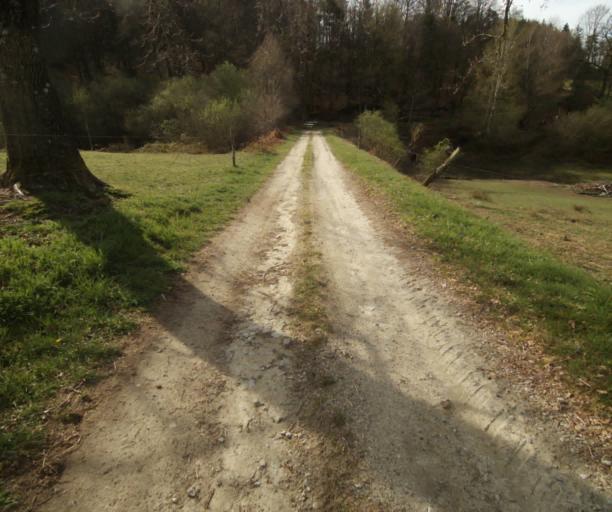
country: FR
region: Limousin
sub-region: Departement de la Correze
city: Correze
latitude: 45.3473
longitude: 1.8647
